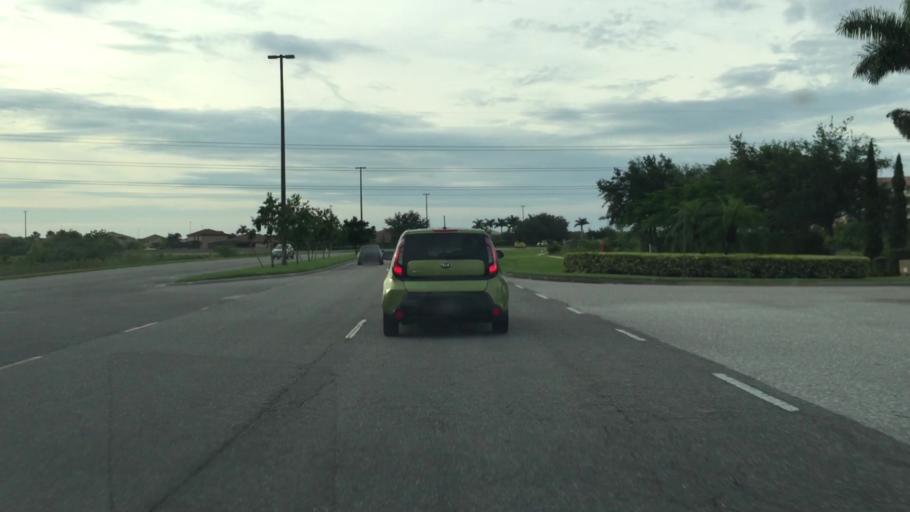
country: US
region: Florida
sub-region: Lee County
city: Fort Myers
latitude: 26.6248
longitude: -81.7932
